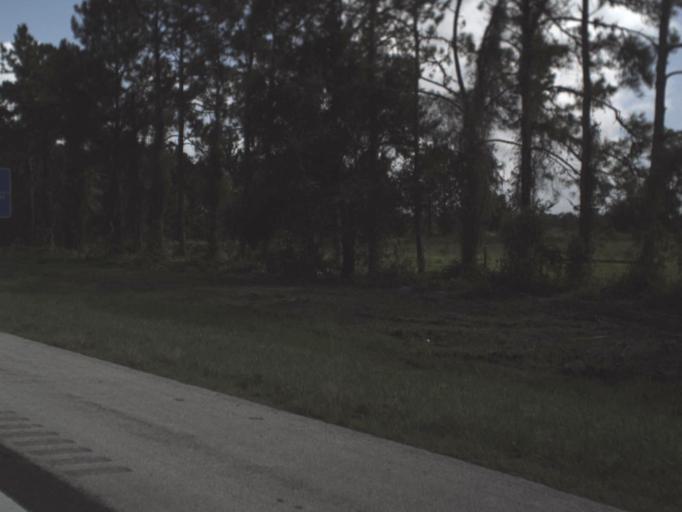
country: US
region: Florida
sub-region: Pasco County
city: San Antonio
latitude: 28.3191
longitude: -82.3249
